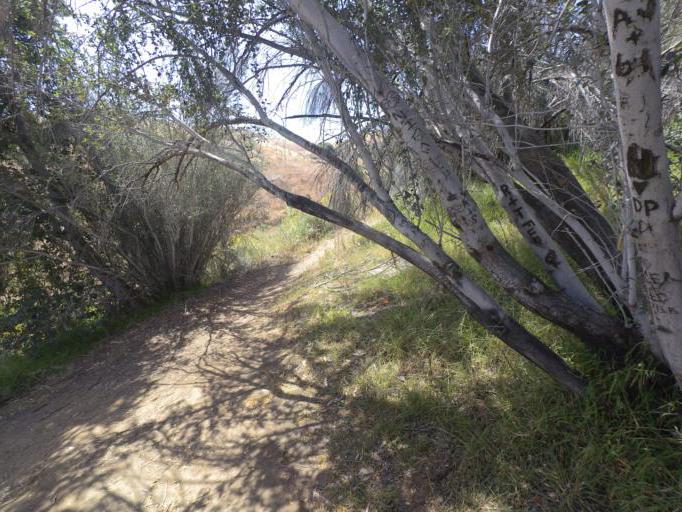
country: US
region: California
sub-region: Riverside County
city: Highgrove
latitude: 33.9680
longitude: -117.3196
